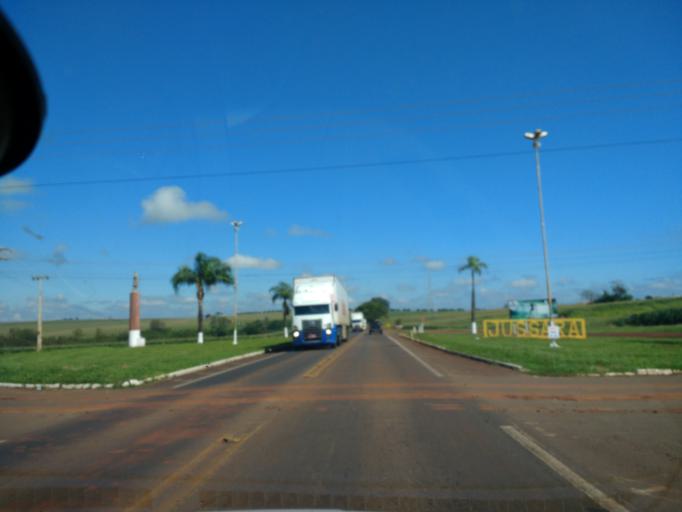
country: BR
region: Parana
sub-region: Terra Boa
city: Terra Boa
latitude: -23.6320
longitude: -52.4639
